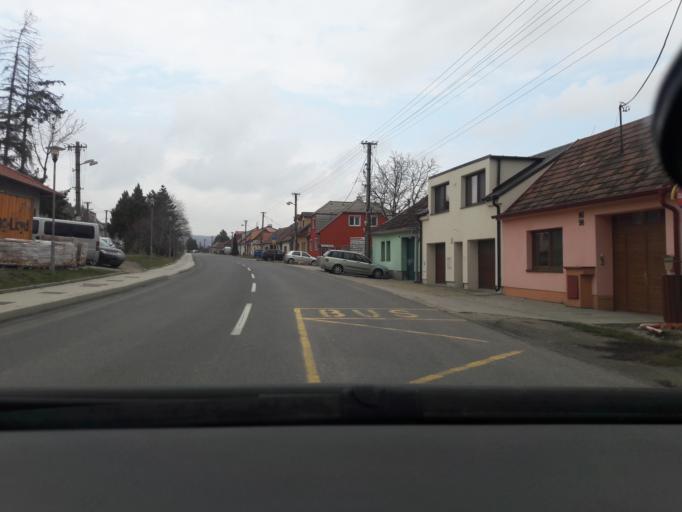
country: SK
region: Bratislavsky
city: Modra
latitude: 48.3961
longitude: 17.3554
